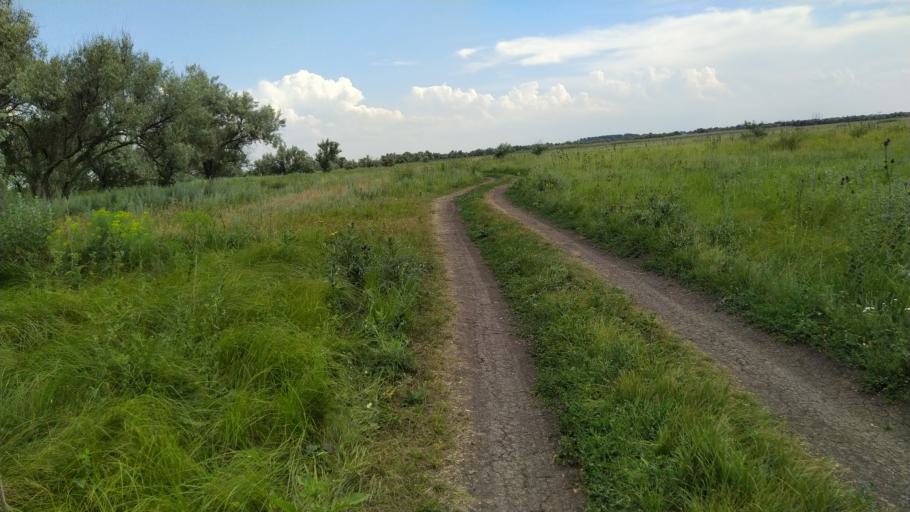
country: RU
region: Rostov
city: Kuleshovka
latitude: 47.1307
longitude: 39.6295
